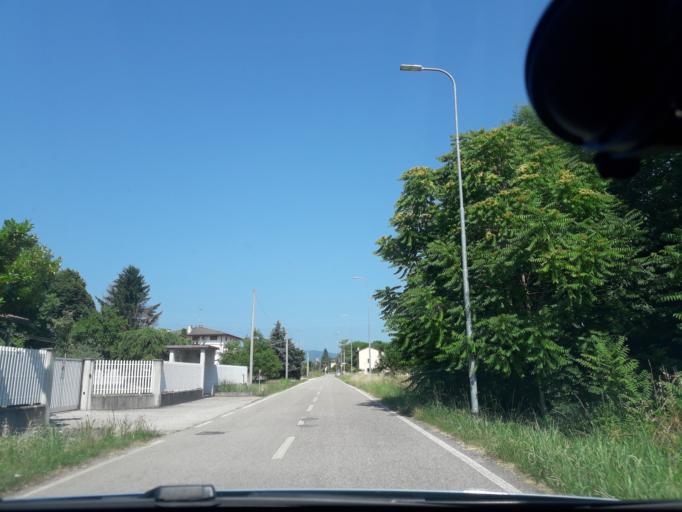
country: IT
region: Friuli Venezia Giulia
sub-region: Provincia di Udine
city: Reana del Rojale
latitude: 46.1127
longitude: 13.2553
